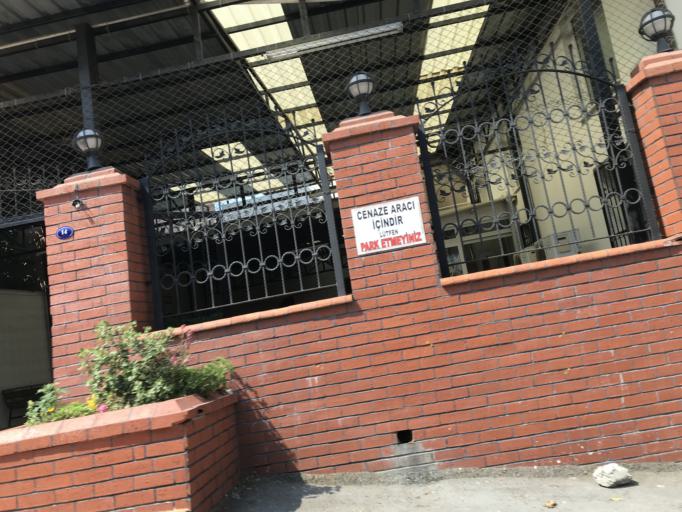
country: TR
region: Izmir
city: Karabaglar
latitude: 38.3885
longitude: 27.1315
